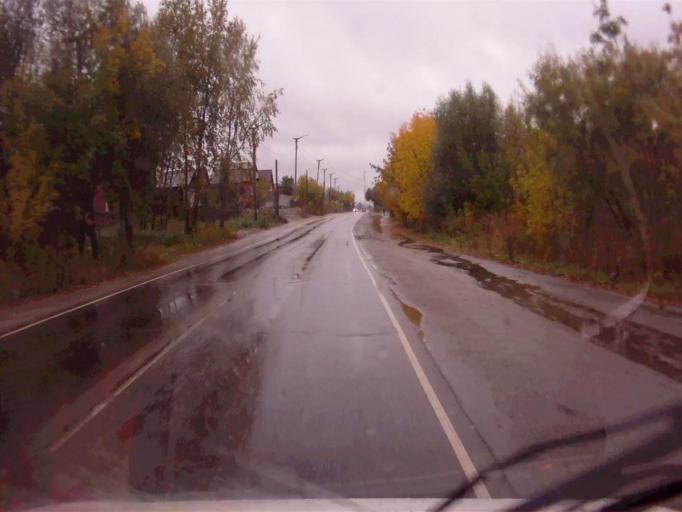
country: RU
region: Chelyabinsk
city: Kyshtym
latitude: 55.7107
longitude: 60.5575
